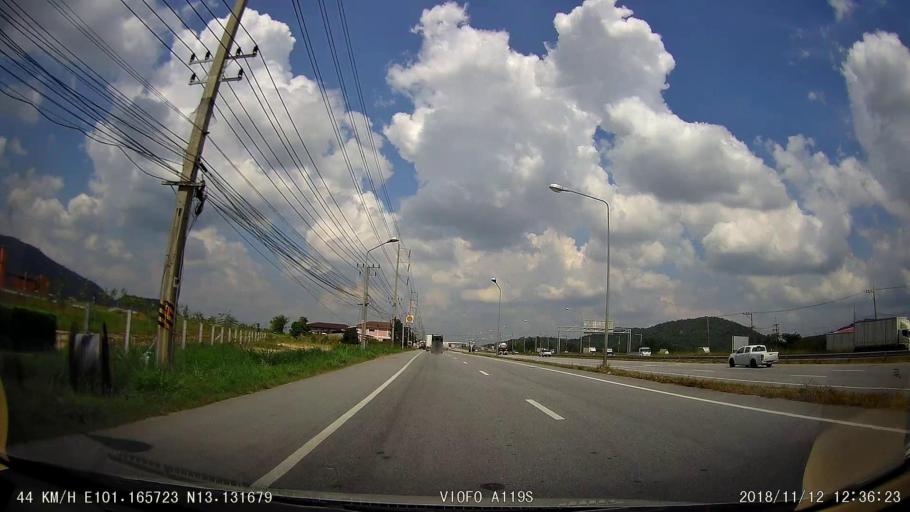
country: TH
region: Rayong
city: Pluak Daeng
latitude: 13.1318
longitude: 101.1658
